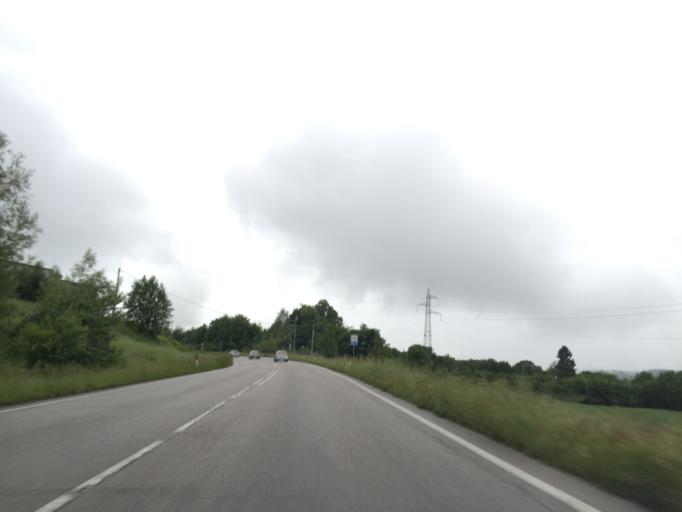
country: IT
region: Veneto
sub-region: Provincia di Belluno
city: Limana
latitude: 46.1012
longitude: 12.1765
